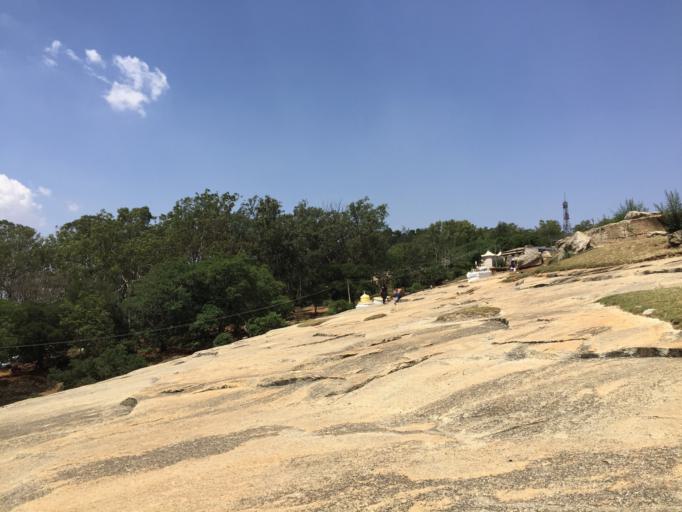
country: IN
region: Karnataka
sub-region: Chikkaballapur
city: Chik Ballapur
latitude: 13.3683
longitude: 77.6824
